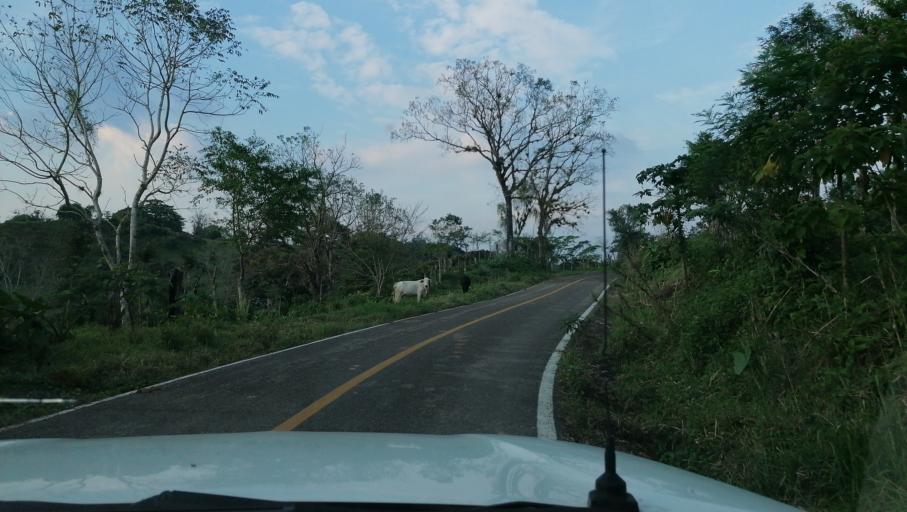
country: MX
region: Chiapas
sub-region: Juarez
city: El Triunfo 1ra. Seccion (Cardona)
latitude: 17.5011
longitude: -93.2452
